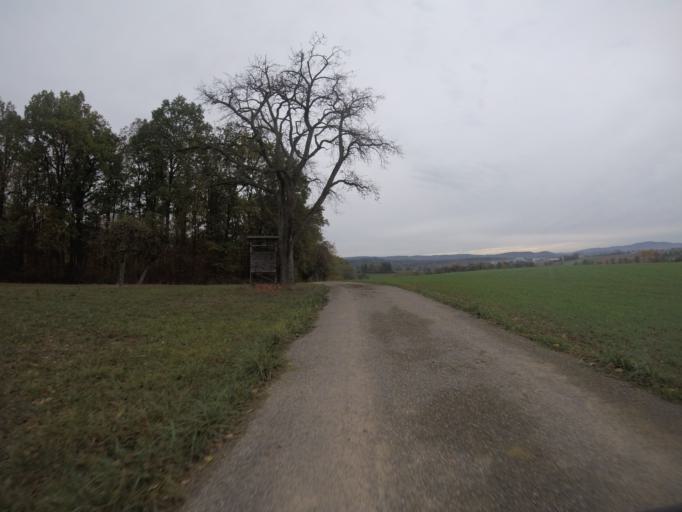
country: DE
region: Baden-Wuerttemberg
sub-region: Regierungsbezirk Stuttgart
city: Aspach
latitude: 48.9666
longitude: 9.3676
